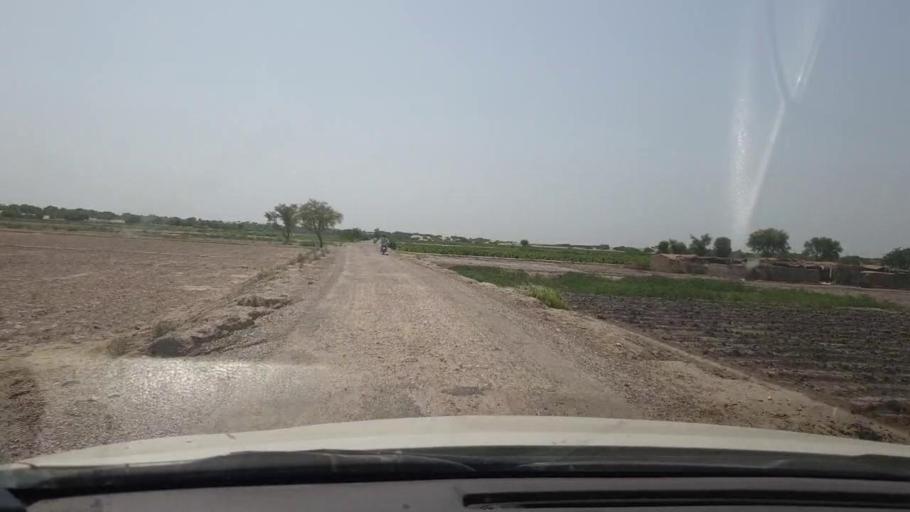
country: PK
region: Sindh
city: Rohri
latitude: 27.5184
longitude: 69.0833
